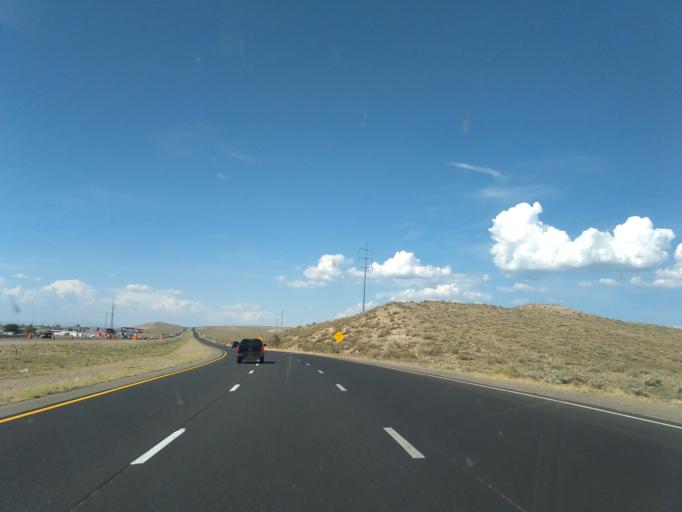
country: US
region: New Mexico
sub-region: Bernalillo County
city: South Valley
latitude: 34.9566
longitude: -106.6591
